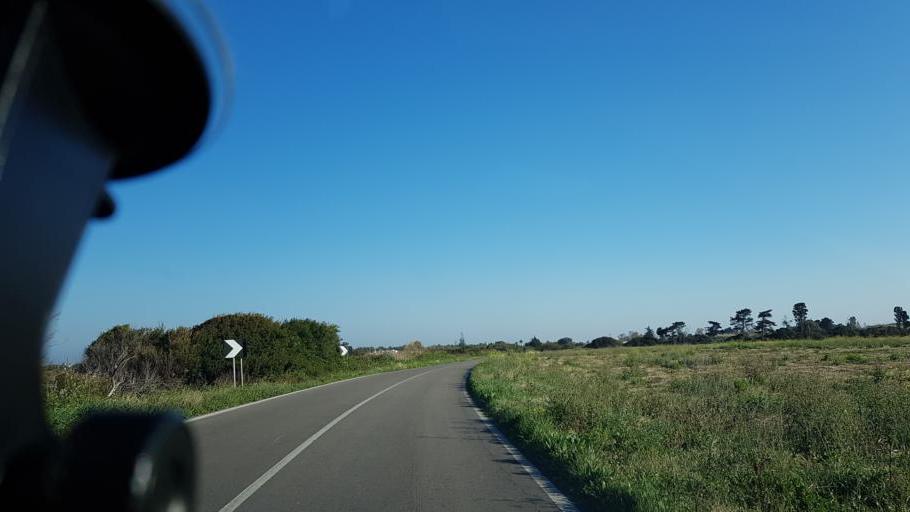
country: IT
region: Apulia
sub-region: Provincia di Lecce
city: Giorgilorio
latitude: 40.4371
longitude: 18.2386
